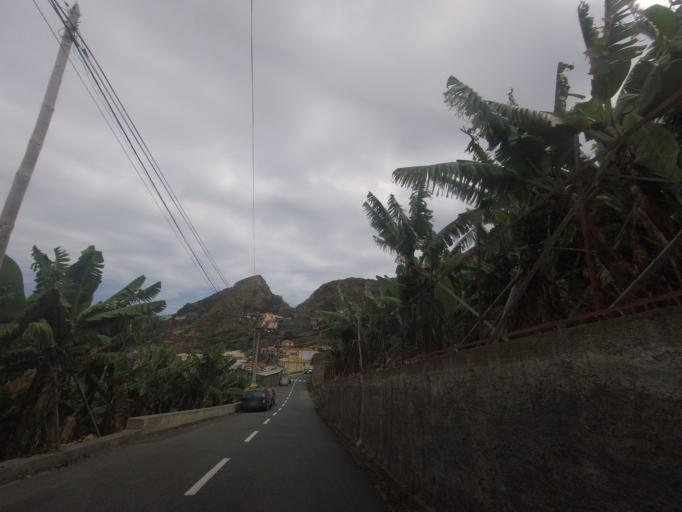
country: PT
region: Madeira
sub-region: Ribeira Brava
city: Campanario
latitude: 32.6587
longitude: -16.9975
